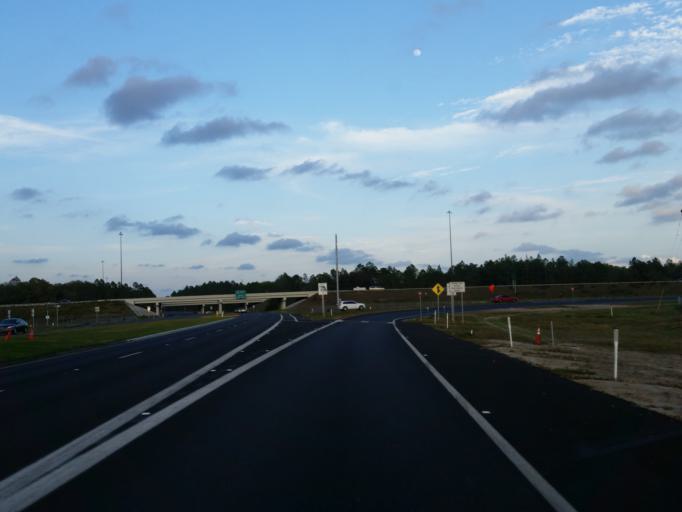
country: US
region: Florida
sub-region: Hillsborough County
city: Temple Terrace
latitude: 28.0692
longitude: -82.3570
